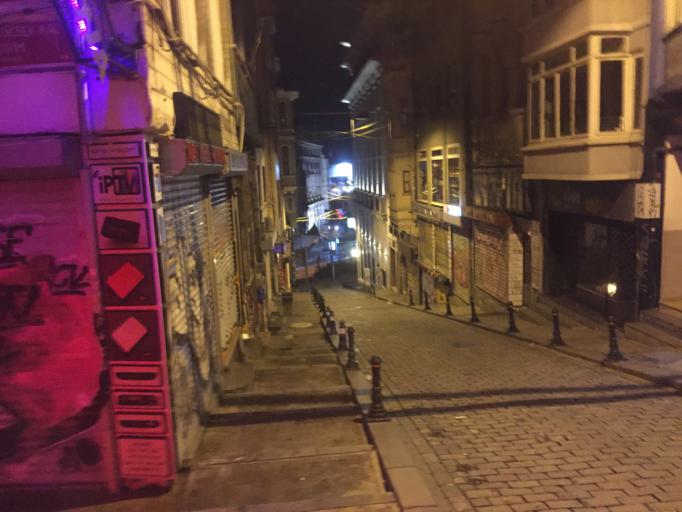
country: TR
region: Istanbul
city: Eminoenue
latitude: 41.0244
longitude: 28.9749
